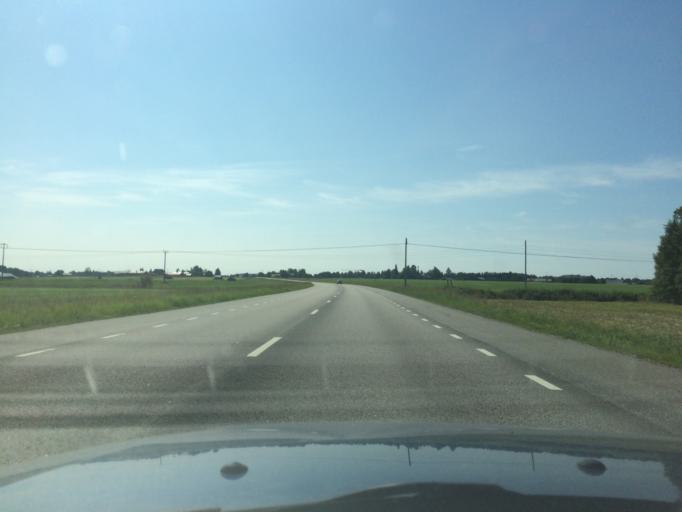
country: SE
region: Norrbotten
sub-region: Pitea Kommun
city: Norrfjarden
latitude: 65.3638
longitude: 21.4073
